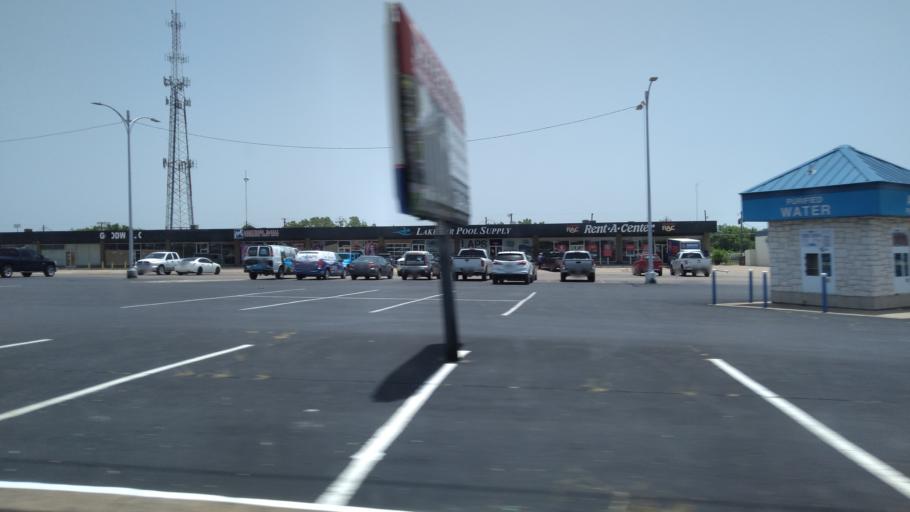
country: US
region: Texas
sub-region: McLennan County
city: Beverly Hills
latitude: 31.5322
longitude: -97.1578
